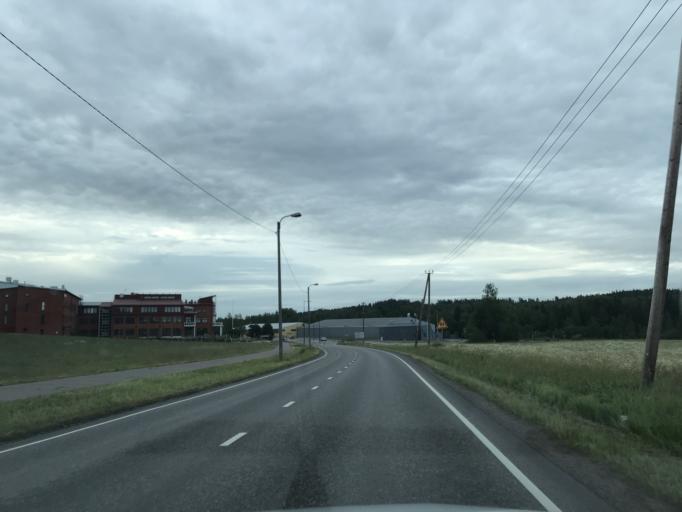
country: FI
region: Uusimaa
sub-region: Helsinki
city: Nurmijaervi
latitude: 60.3806
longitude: 24.7340
